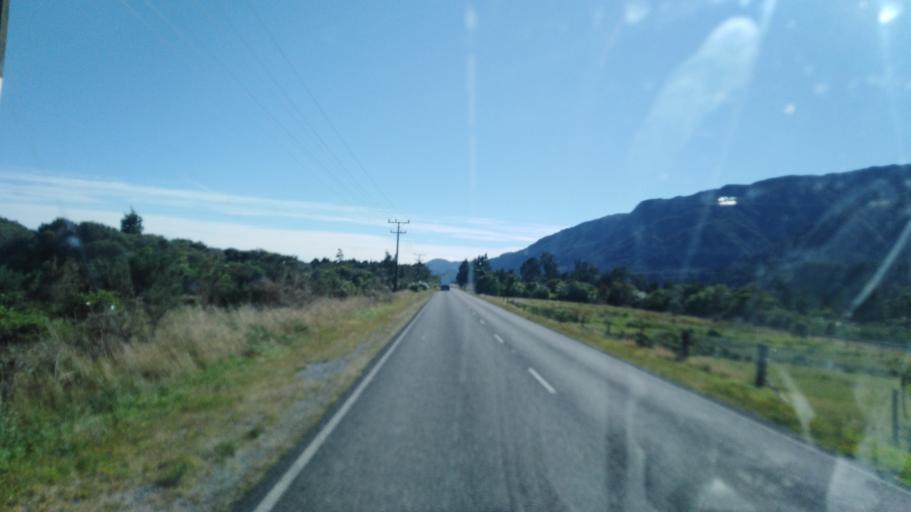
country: NZ
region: West Coast
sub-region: Buller District
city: Westport
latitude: -41.6712
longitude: 171.8043
